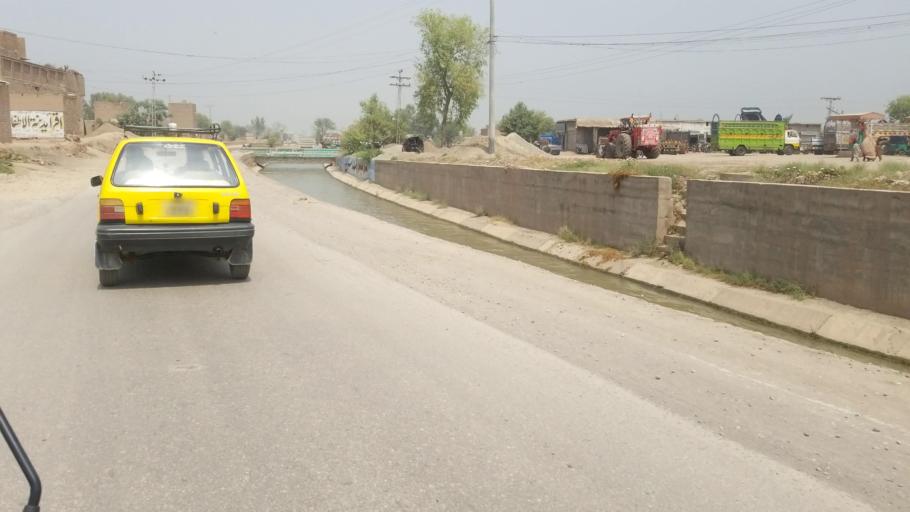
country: PK
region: Khyber Pakhtunkhwa
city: Peshawar
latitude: 33.9614
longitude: 71.5426
